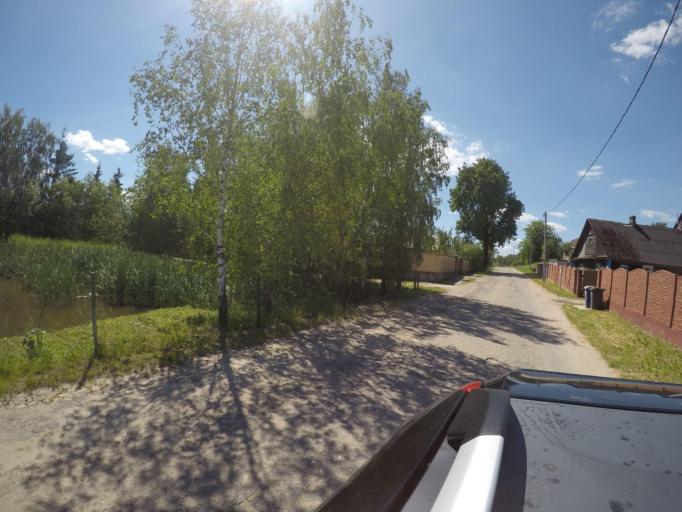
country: BY
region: Grodnenskaya
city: Hrodna
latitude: 53.7282
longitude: 23.8506
